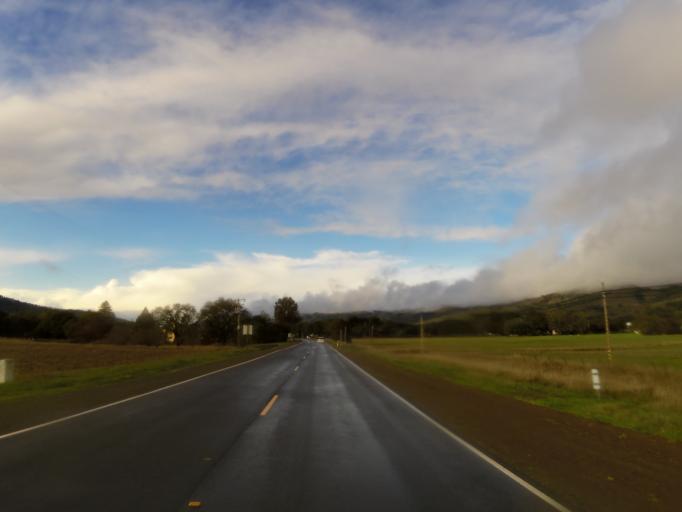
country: US
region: California
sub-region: Mendocino County
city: Boonville
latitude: 38.9962
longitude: -123.3564
